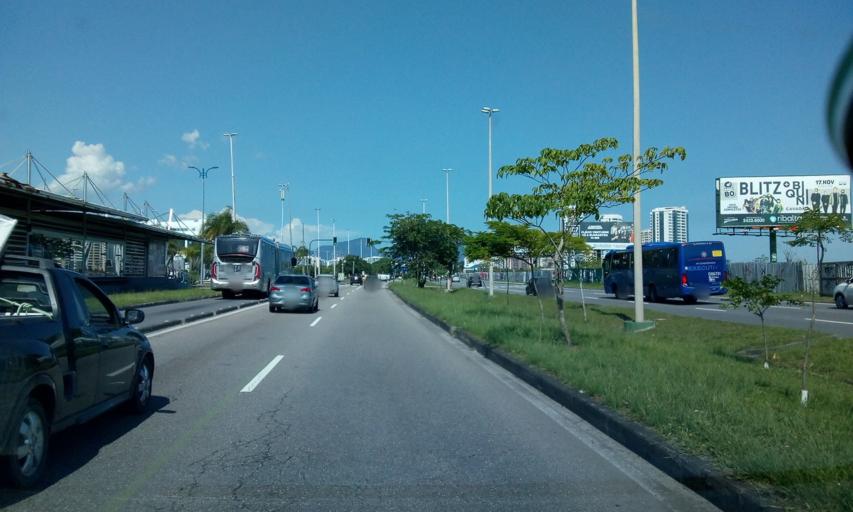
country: BR
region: Rio de Janeiro
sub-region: Nilopolis
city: Nilopolis
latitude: -23.0002
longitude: -43.4125
